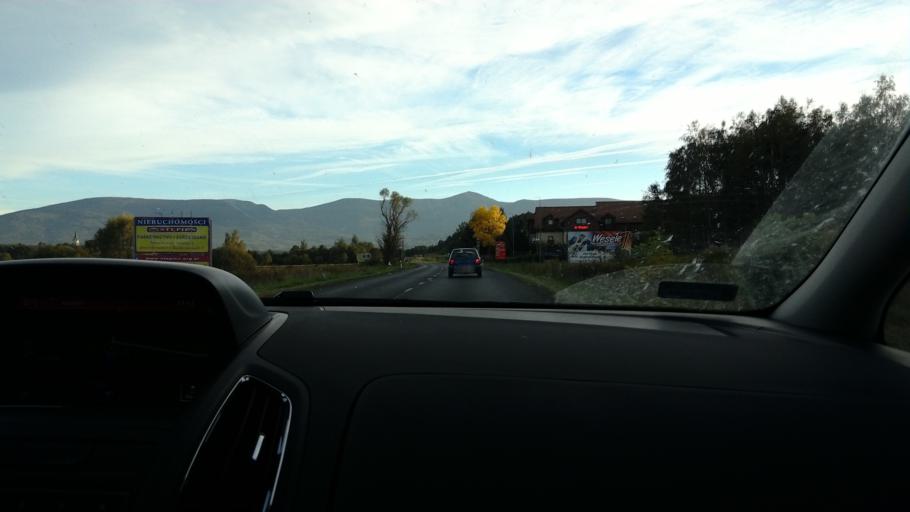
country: PL
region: Lower Silesian Voivodeship
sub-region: Powiat jeleniogorski
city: Myslakowice
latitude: 50.8535
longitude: 15.7741
